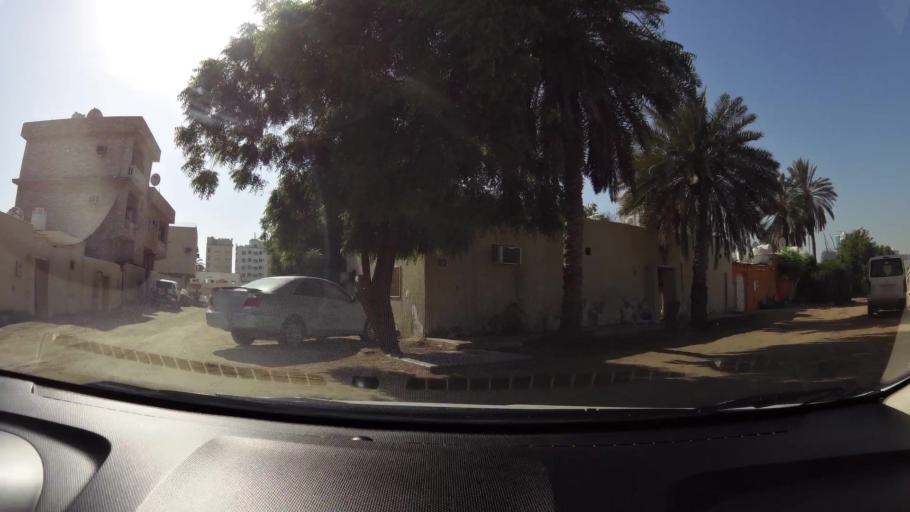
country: AE
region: Ajman
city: Ajman
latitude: 25.4130
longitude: 55.4500
